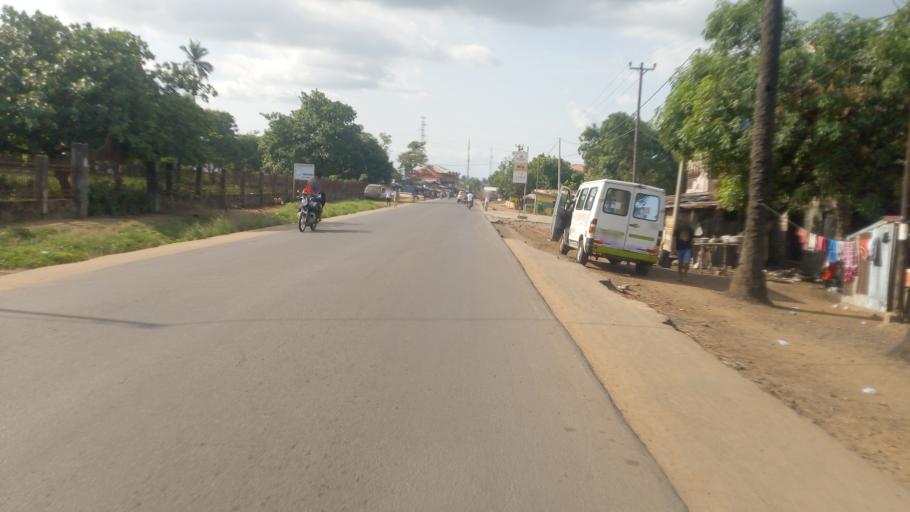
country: SL
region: Western Area
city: Waterloo
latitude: 8.3239
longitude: -13.0725
